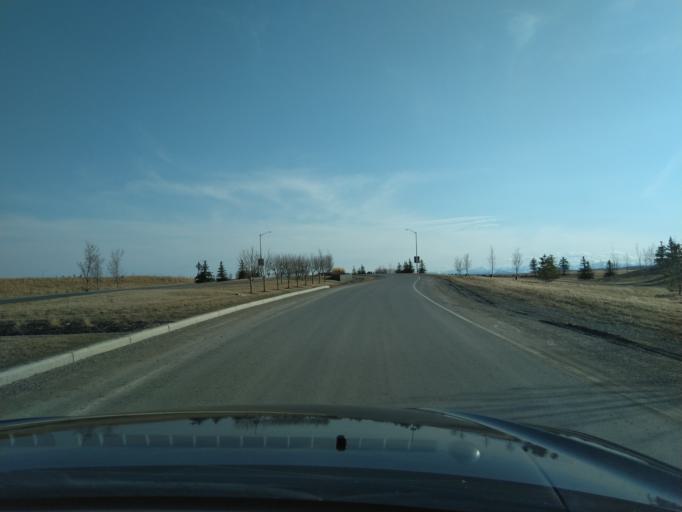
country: CA
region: Alberta
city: Cochrane
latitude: 51.1087
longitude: -114.3915
